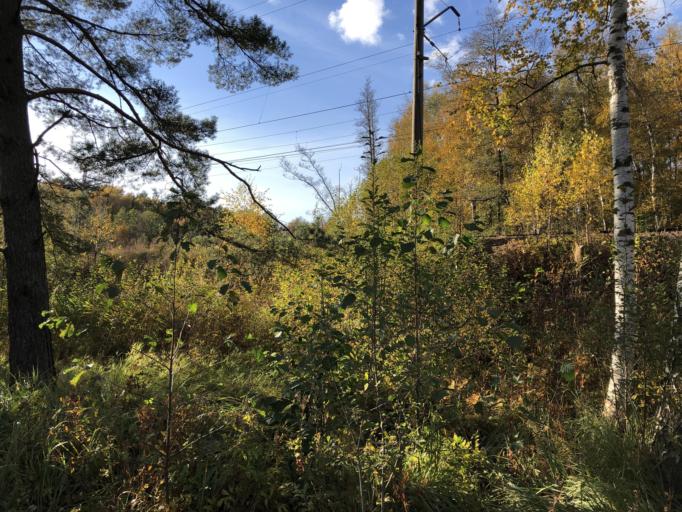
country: LV
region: Carnikava
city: Carnikava
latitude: 57.1449
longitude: 24.2950
